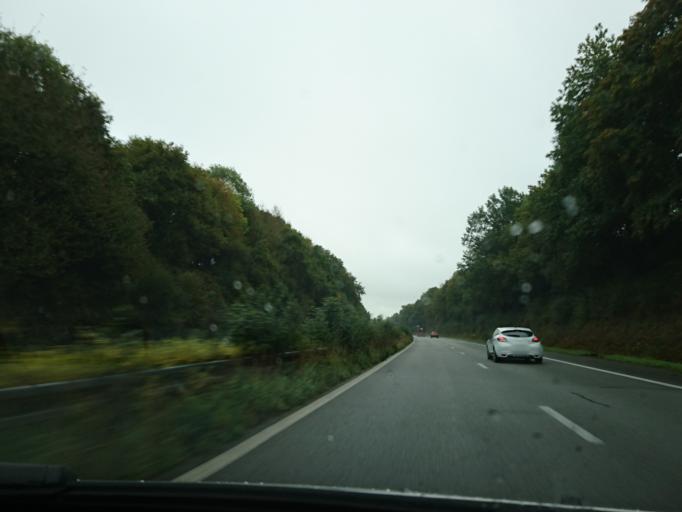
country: FR
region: Brittany
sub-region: Departement du Finistere
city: Quimperle
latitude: 47.8626
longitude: -3.5672
